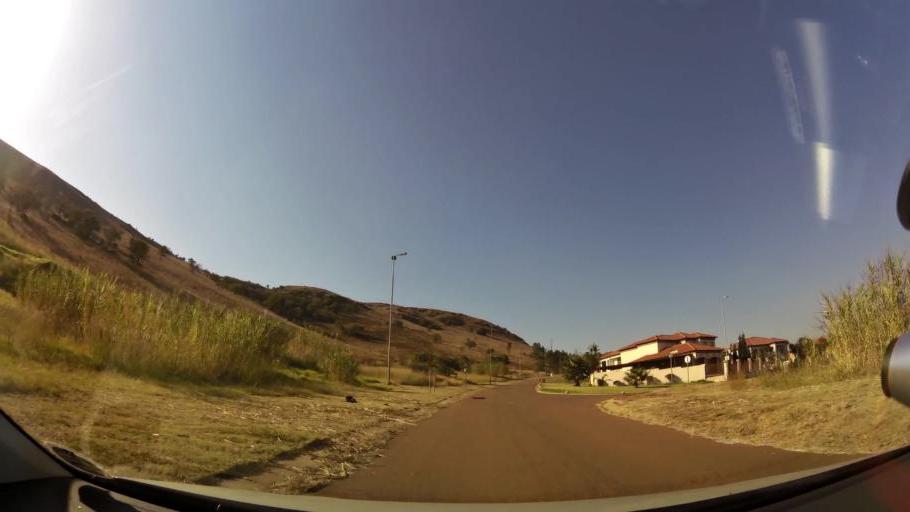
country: ZA
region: Gauteng
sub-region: City of Tshwane Metropolitan Municipality
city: Pretoria
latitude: -25.6923
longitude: 28.1302
